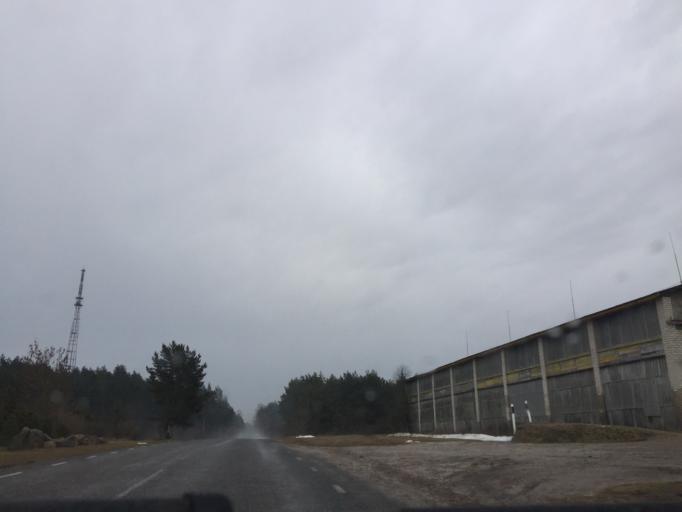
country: EE
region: Saare
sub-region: Orissaare vald
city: Orissaare
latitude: 58.5604
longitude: 23.0543
